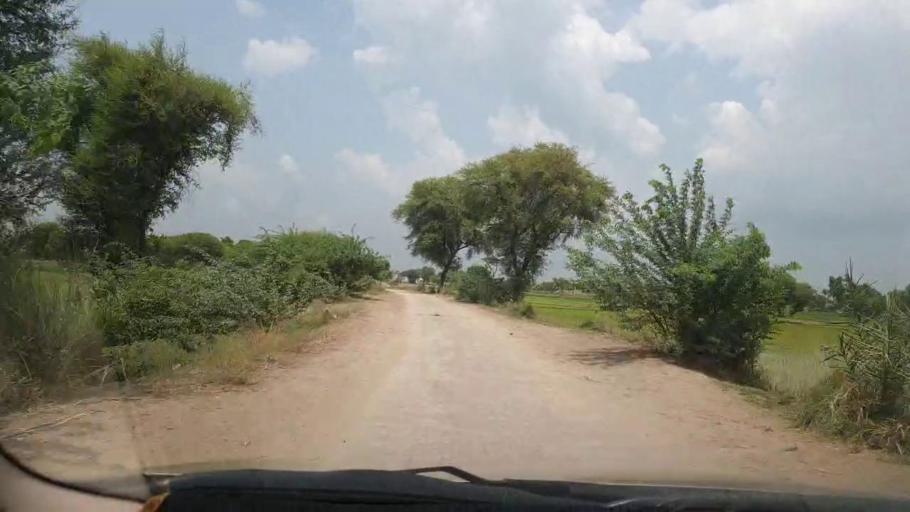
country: PK
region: Sindh
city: Larkana
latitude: 27.5725
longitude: 68.1237
